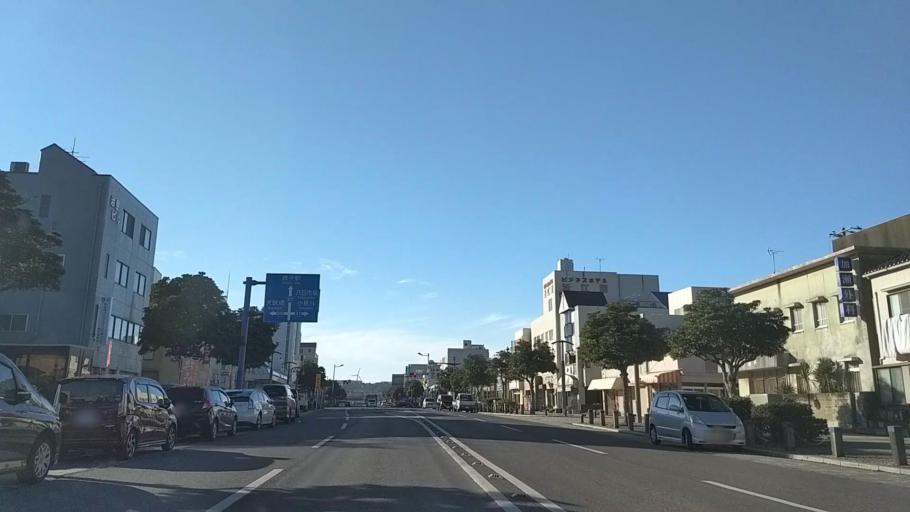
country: JP
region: Chiba
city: Hasaki
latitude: 35.7335
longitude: 140.8284
